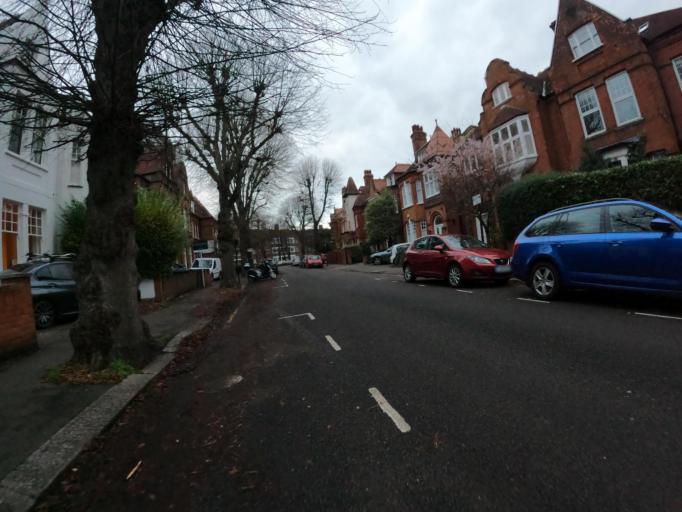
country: GB
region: England
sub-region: Greater London
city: Acton
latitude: 51.4910
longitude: -0.2740
